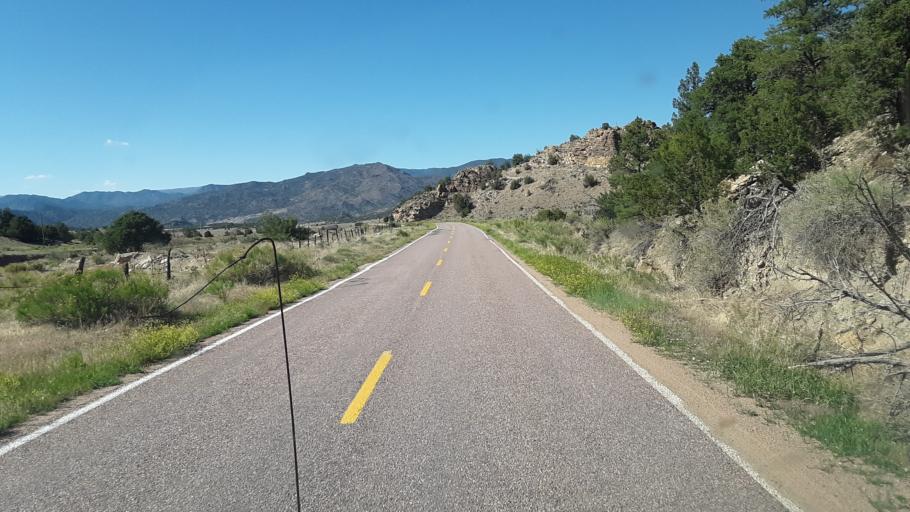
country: US
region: Colorado
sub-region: Fremont County
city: Canon City
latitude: 38.4463
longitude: -105.3735
